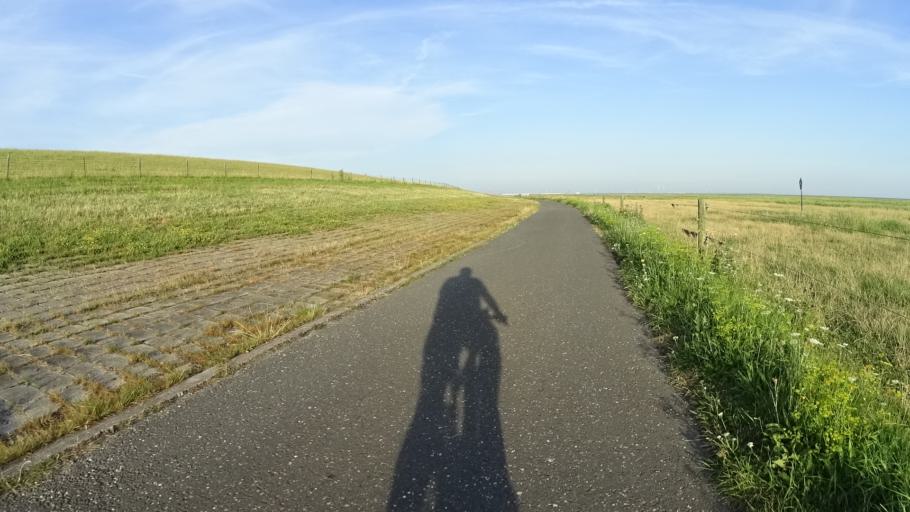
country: DE
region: Lower Saxony
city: Butjadingen
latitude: 53.6084
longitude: 8.2908
